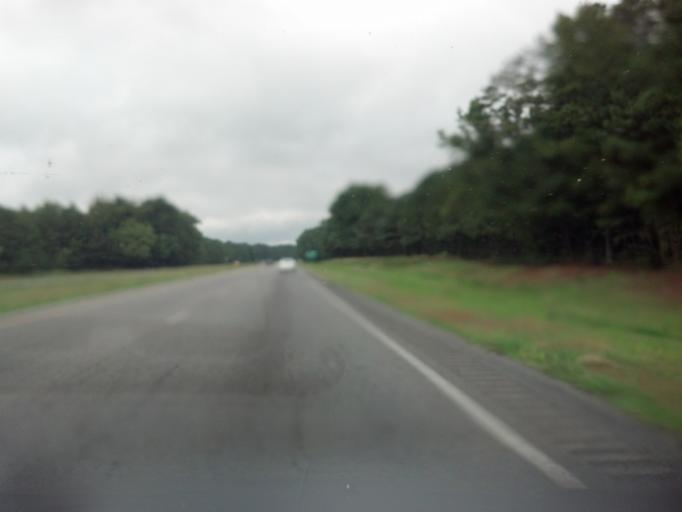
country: US
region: North Carolina
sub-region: Nash County
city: Rocky Mount
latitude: 35.9359
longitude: -77.7357
